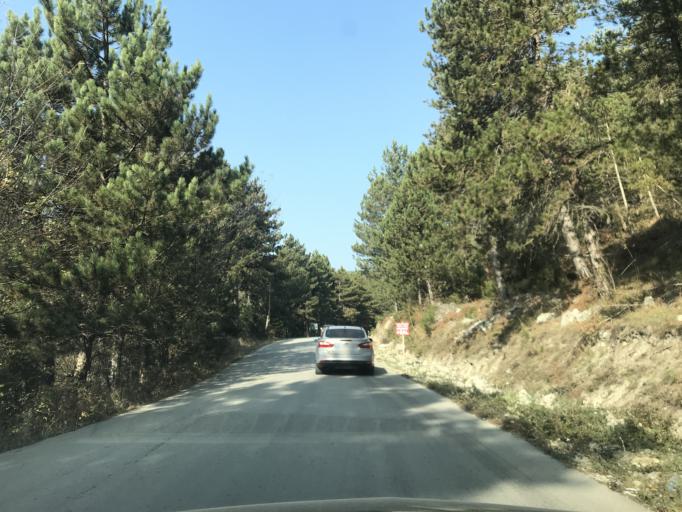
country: TR
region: Bolu
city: Bolu
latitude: 40.7840
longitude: 31.6327
